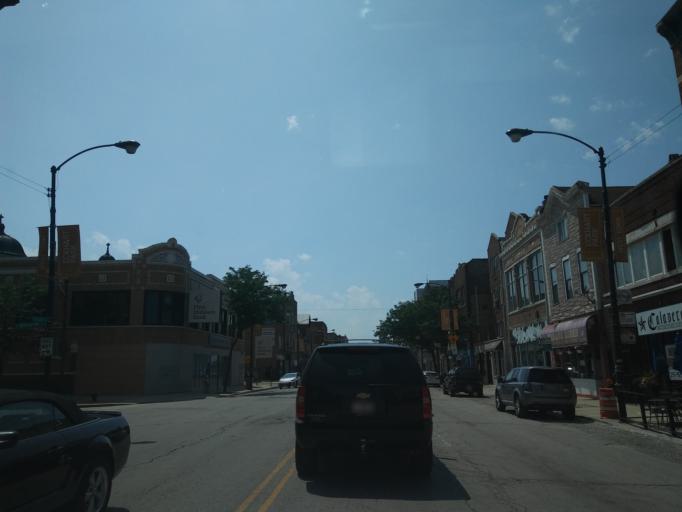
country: US
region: Illinois
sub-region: Cook County
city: Chicago
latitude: 41.8962
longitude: -87.6636
